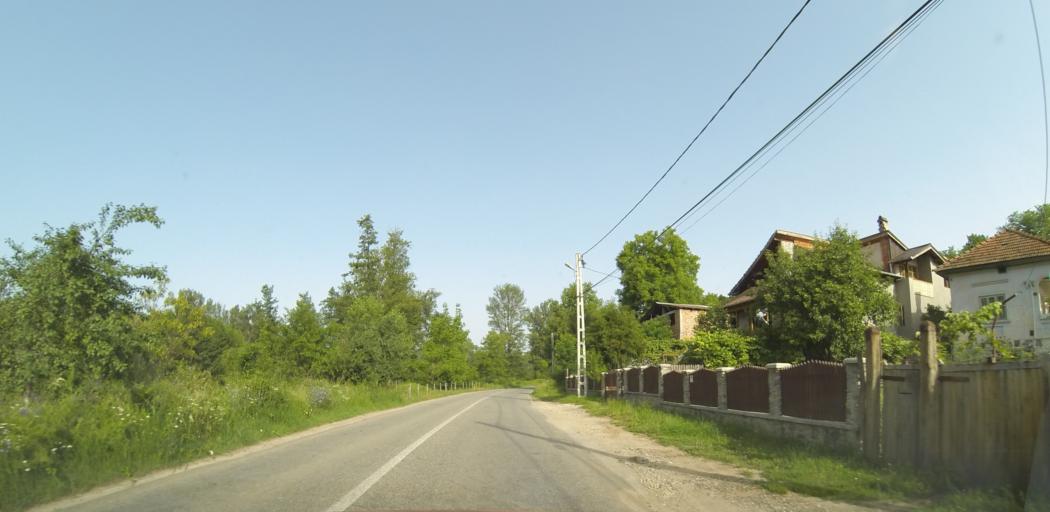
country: RO
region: Valcea
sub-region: Comuna Pausesti-Maglasi
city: Pausesti-Maglasi
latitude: 45.1303
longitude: 24.2625
